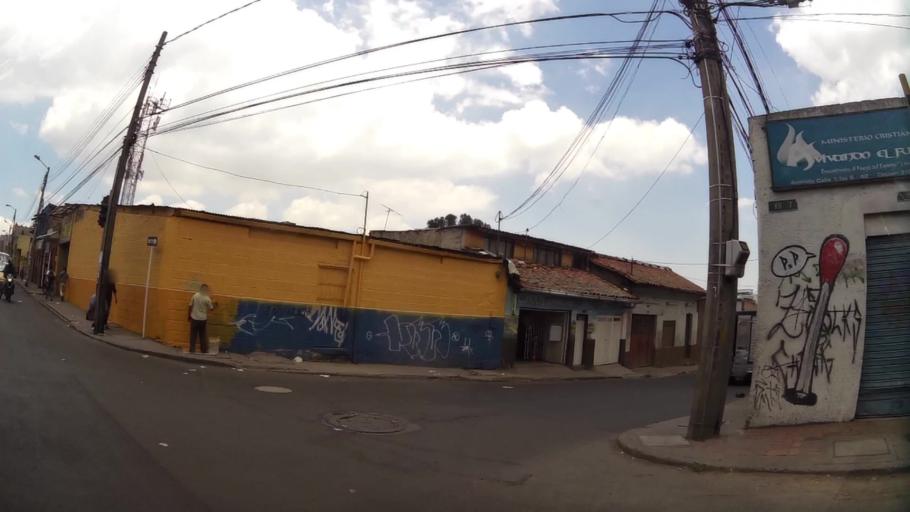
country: CO
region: Bogota D.C.
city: Bogota
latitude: 4.5867
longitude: -74.0818
